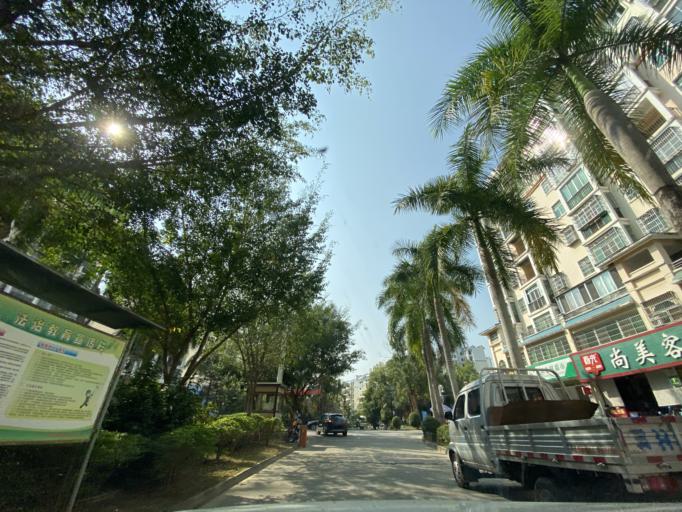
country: CN
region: Hainan
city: Chongshan
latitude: 18.7683
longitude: 109.5244
